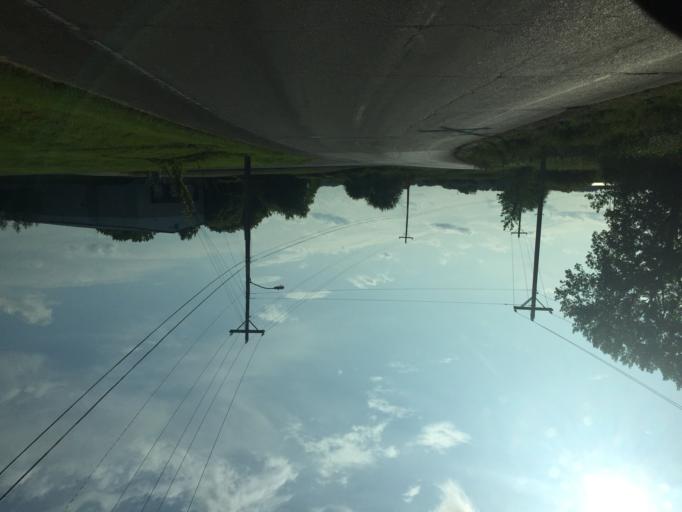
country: US
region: Minnesota
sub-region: Olmsted County
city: Rochester
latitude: 44.0361
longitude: -92.4996
